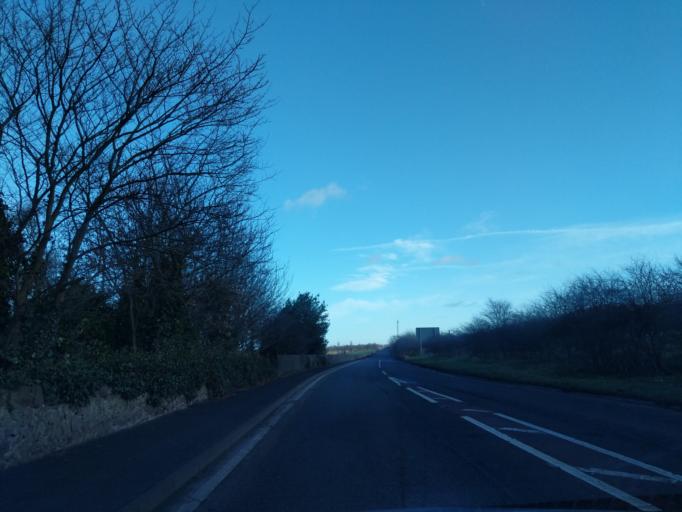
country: GB
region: Scotland
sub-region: East Lothian
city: East Linton
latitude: 55.9862
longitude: -2.6420
